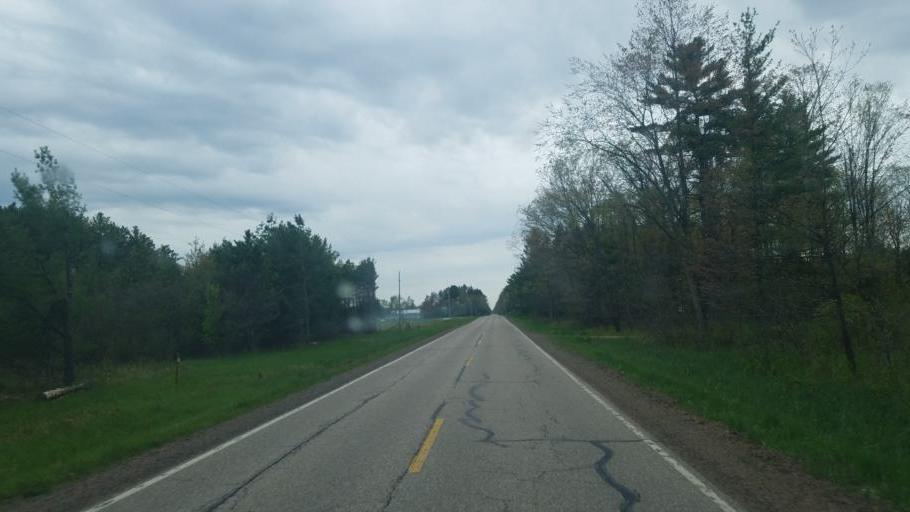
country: US
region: Wisconsin
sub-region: Wood County
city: Marshfield
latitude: 44.5188
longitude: -90.2994
